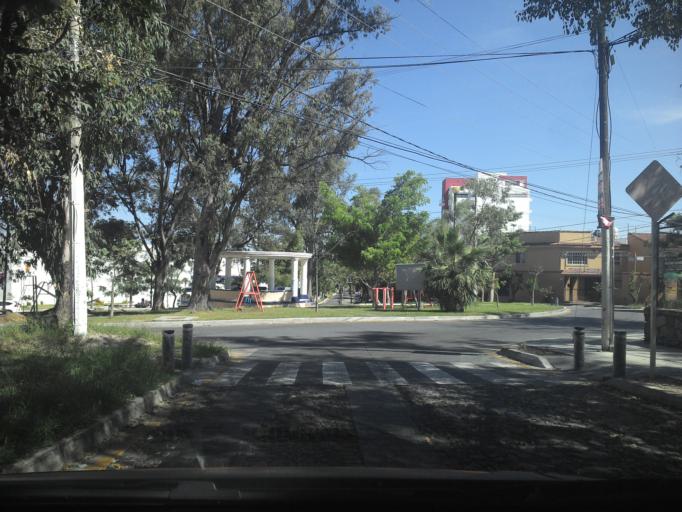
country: MX
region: Jalisco
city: Guadalajara
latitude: 20.6703
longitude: -103.4508
